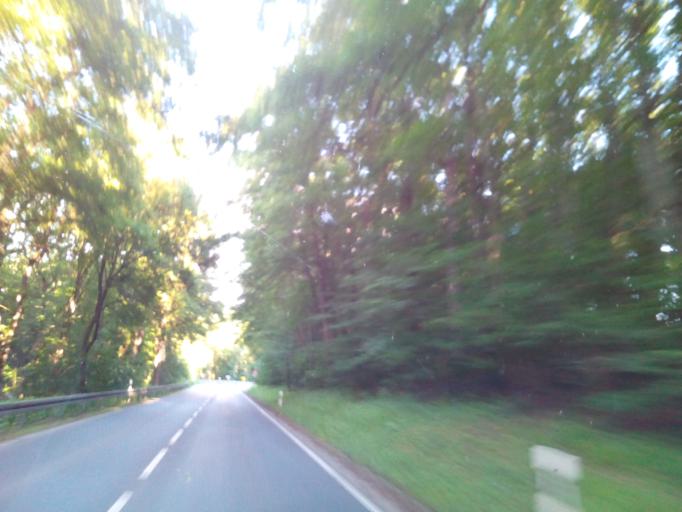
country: DE
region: Bavaria
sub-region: Regierungsbezirk Unterfranken
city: Nudlingen
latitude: 50.2162
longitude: 10.1094
